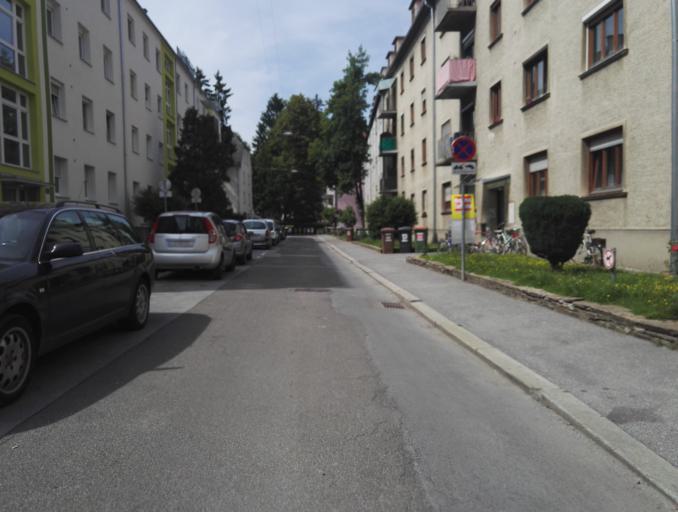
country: AT
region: Styria
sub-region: Graz Stadt
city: Wetzelsdorf
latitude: 47.0498
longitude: 15.4268
